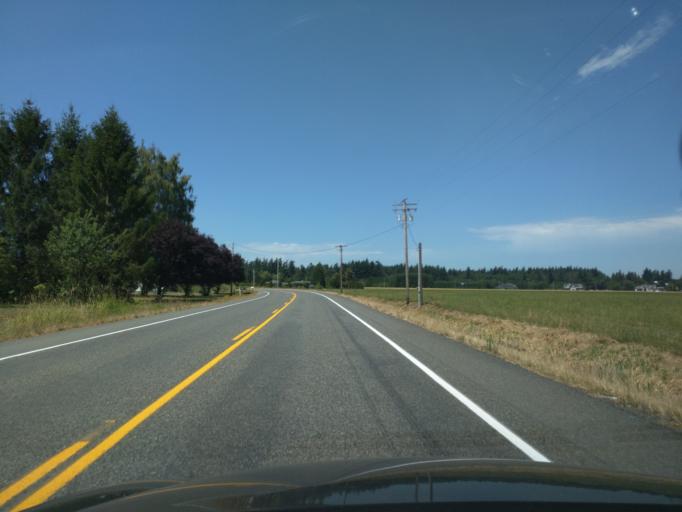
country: US
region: Washington
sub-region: Whatcom County
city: Lynden
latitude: 48.9651
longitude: -122.4941
